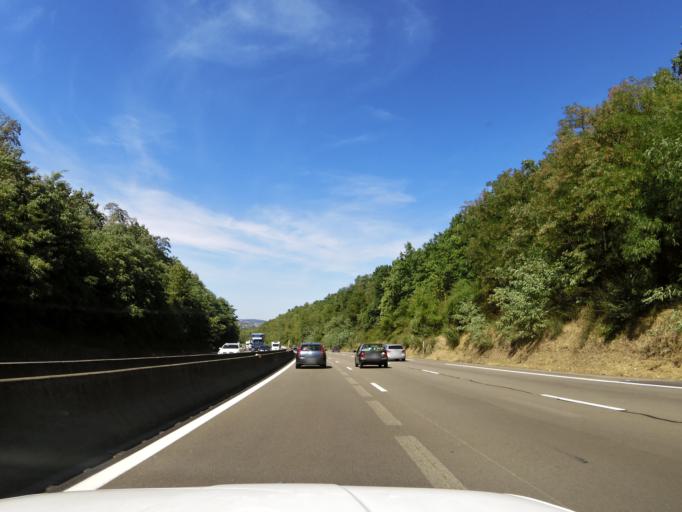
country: FR
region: Rhone-Alpes
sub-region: Departement de l'Isere
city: Auberives-sur-Vareze
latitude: 45.4190
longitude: 4.8281
